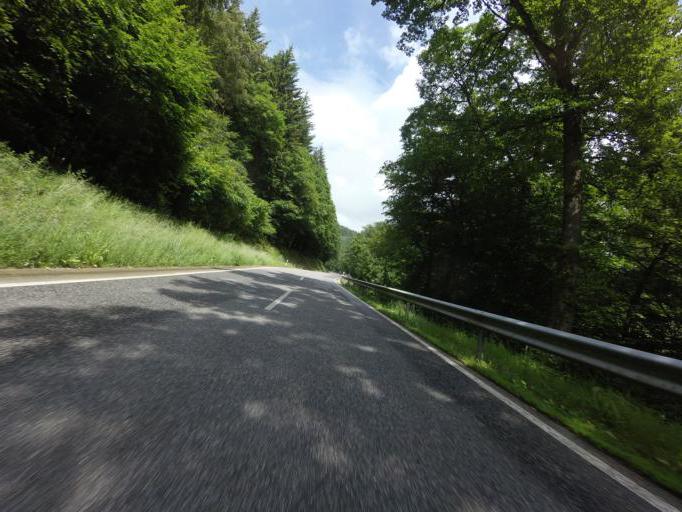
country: DE
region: Rheinland-Pfalz
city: Herschbroich
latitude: 50.3861
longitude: 6.9788
